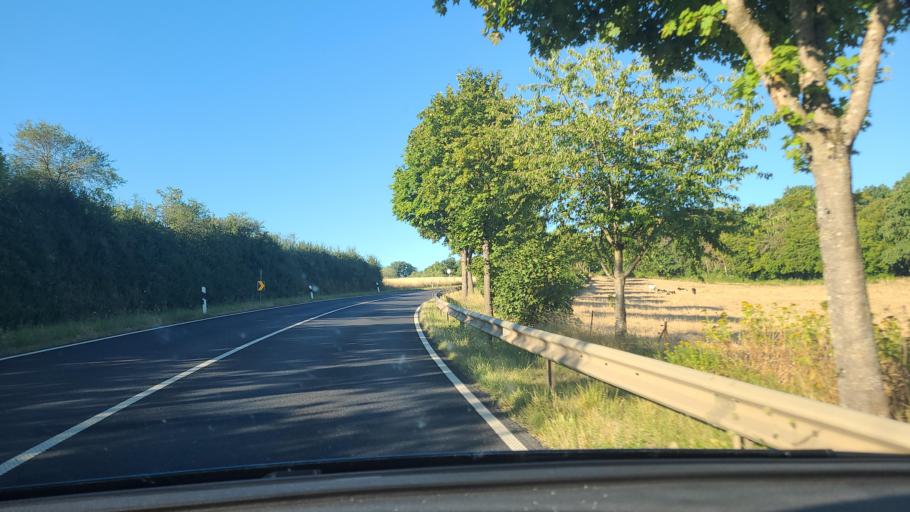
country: LU
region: Luxembourg
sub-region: Canton de Capellen
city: Garnich
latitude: 49.6281
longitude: 5.9561
